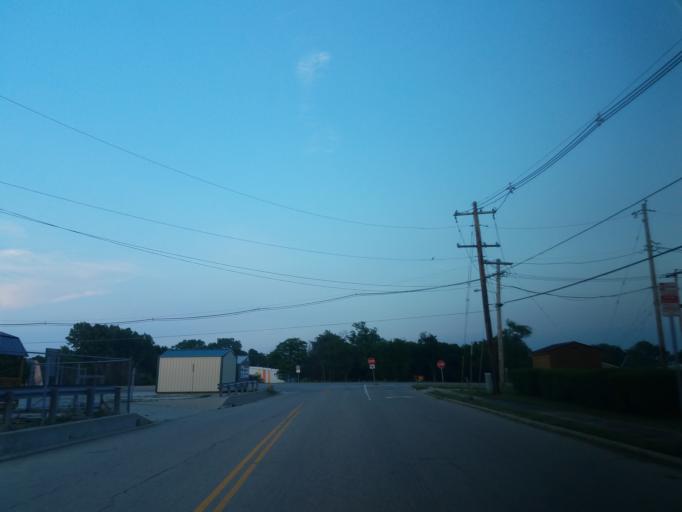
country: US
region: Illinois
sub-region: McLean County
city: Bloomington
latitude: 40.4417
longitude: -88.9919
